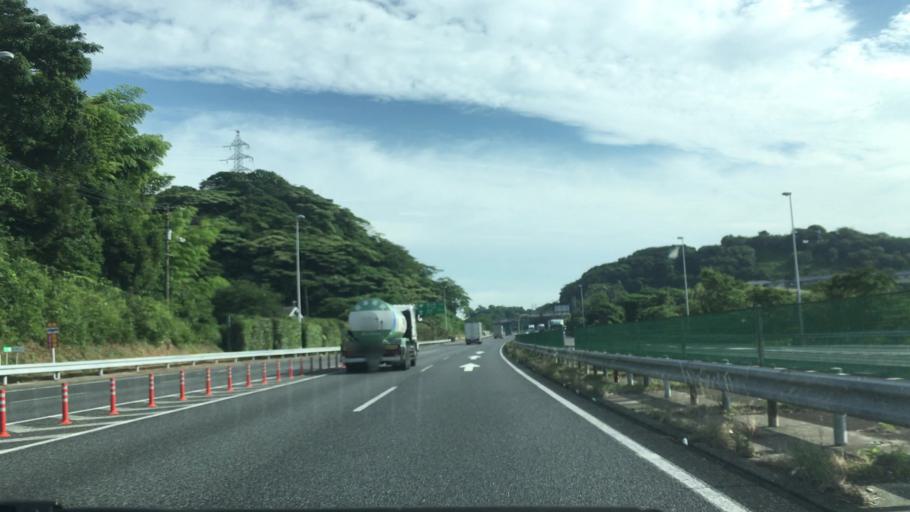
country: JP
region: Yamaguchi
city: Shimonoseki
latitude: 33.9754
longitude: 130.9518
